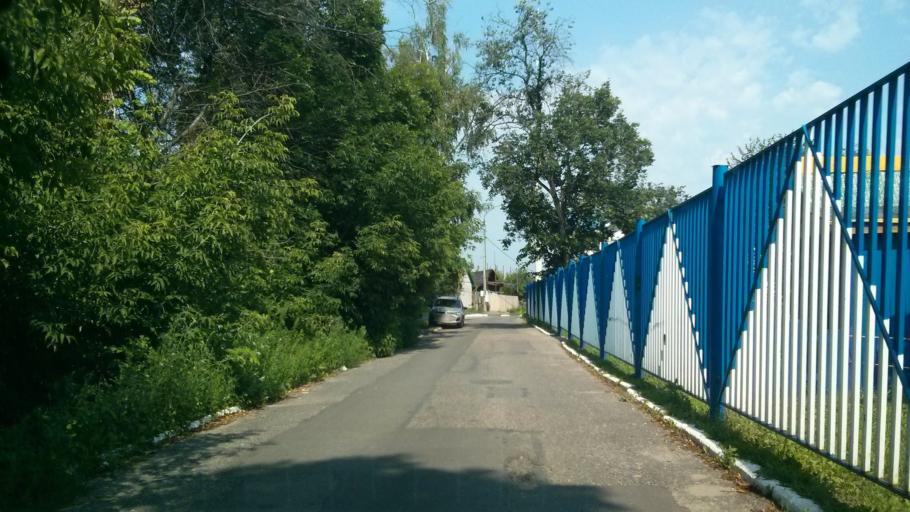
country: RU
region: Vladimir
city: Murom
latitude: 55.5794
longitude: 42.0576
